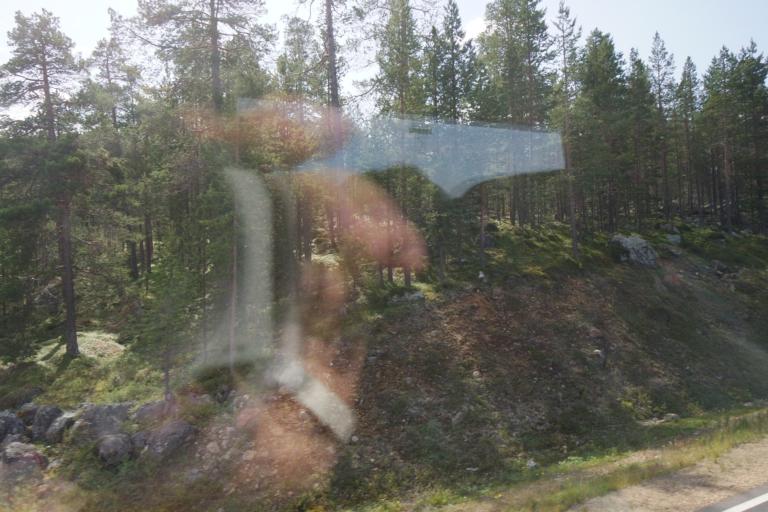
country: FI
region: Lapland
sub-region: Pohjois-Lappi
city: Ivalo
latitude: 68.7810
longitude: 27.4154
